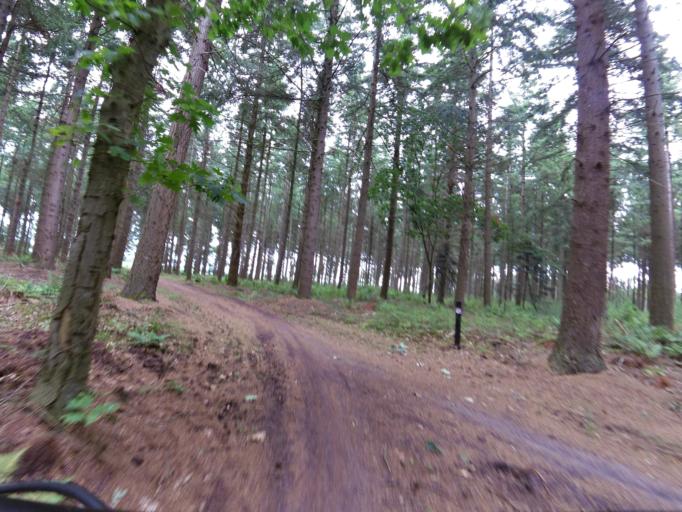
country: NL
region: North Brabant
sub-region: Gemeente Veghel
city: Keldonk
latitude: 51.5481
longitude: 5.5664
